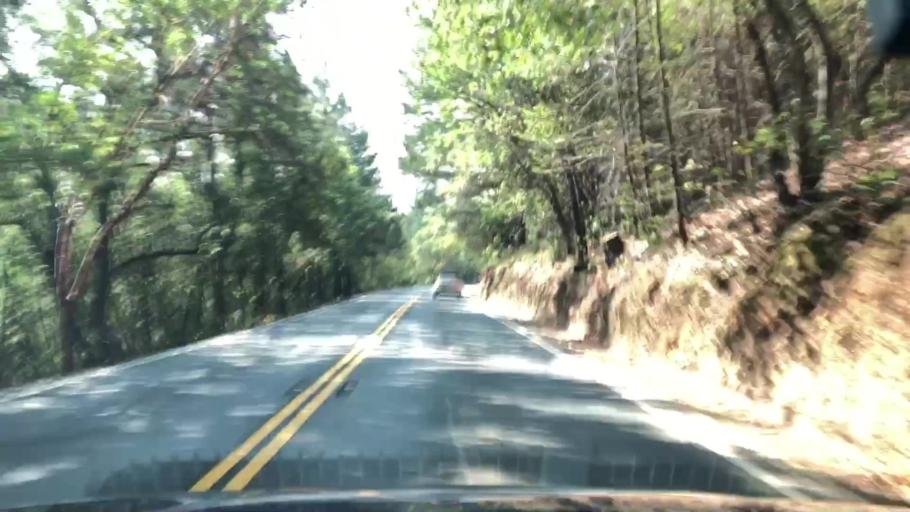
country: US
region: California
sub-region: Napa County
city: Calistoga
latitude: 38.6172
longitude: -122.5969
